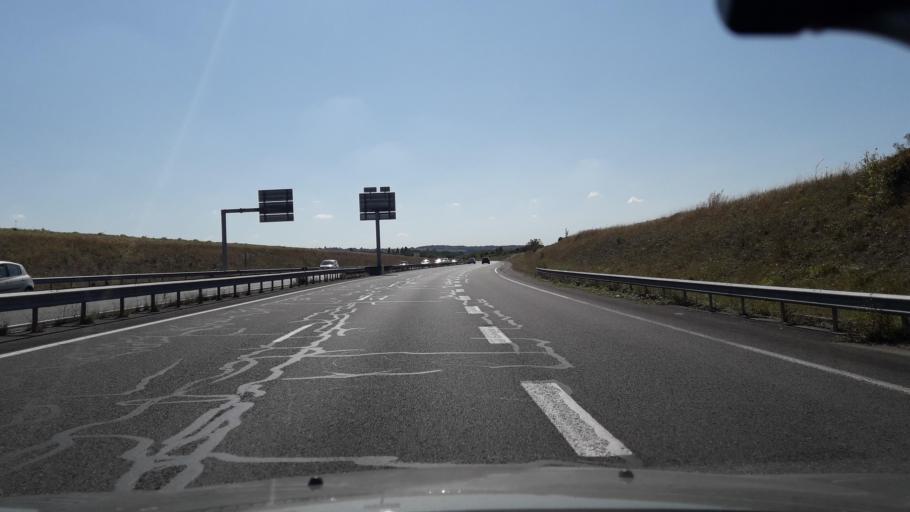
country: FR
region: Poitou-Charentes
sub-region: Departement de la Charente
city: Saint-Meme-les-Carrieres
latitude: 45.6896
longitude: -0.0841
